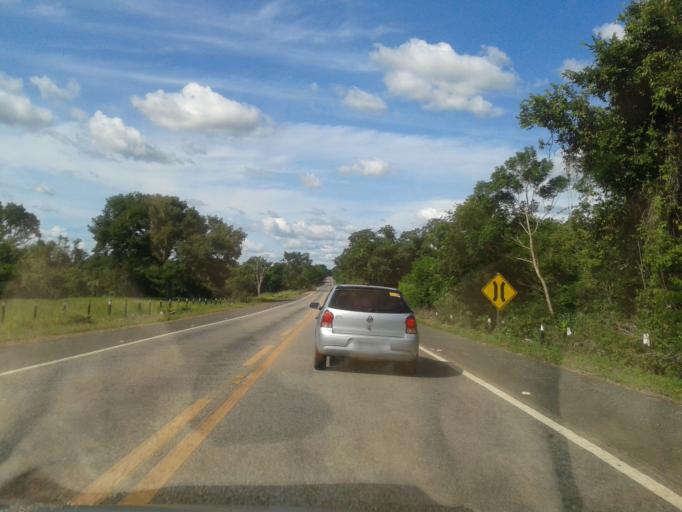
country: BR
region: Goias
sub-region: Mozarlandia
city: Mozarlandia
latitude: -15.0023
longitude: -50.5898
